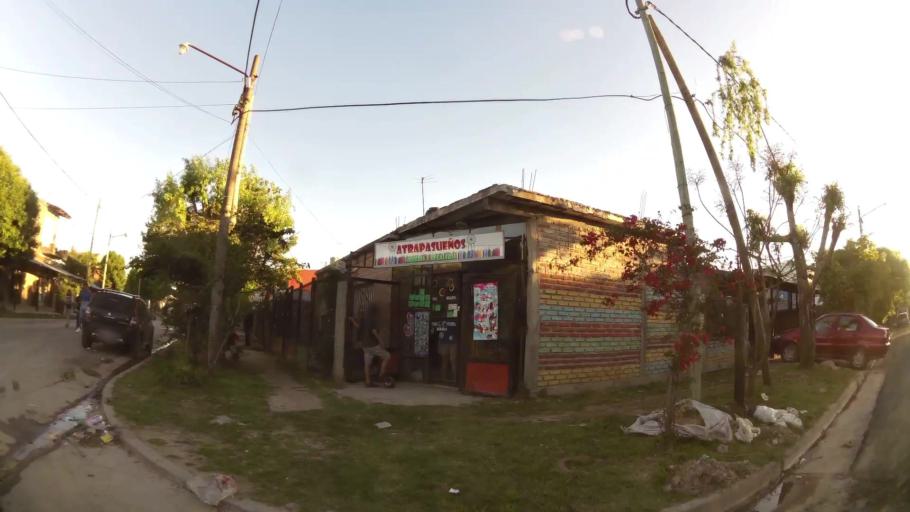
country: AR
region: Buenos Aires
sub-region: Partido de Almirante Brown
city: Adrogue
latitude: -34.7819
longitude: -58.3342
